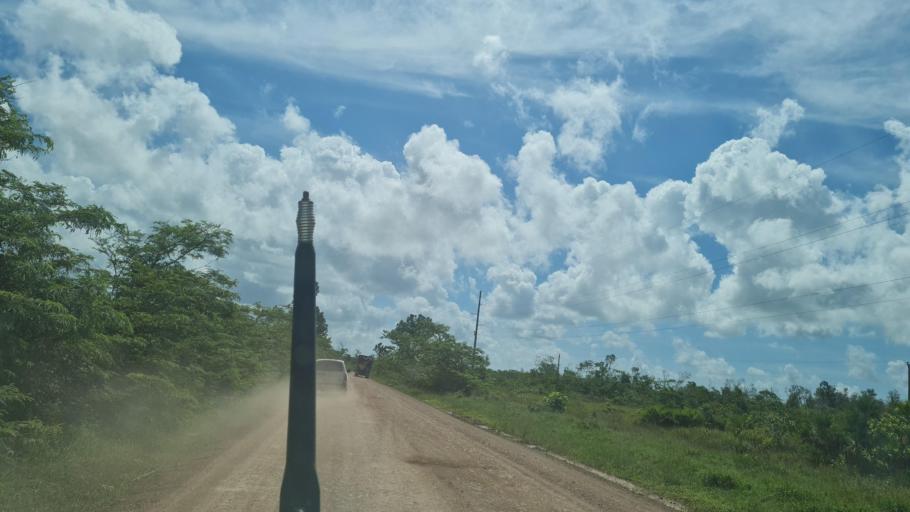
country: NI
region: Atlantico Norte (RAAN)
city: Puerto Cabezas
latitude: 14.1101
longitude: -83.5537
